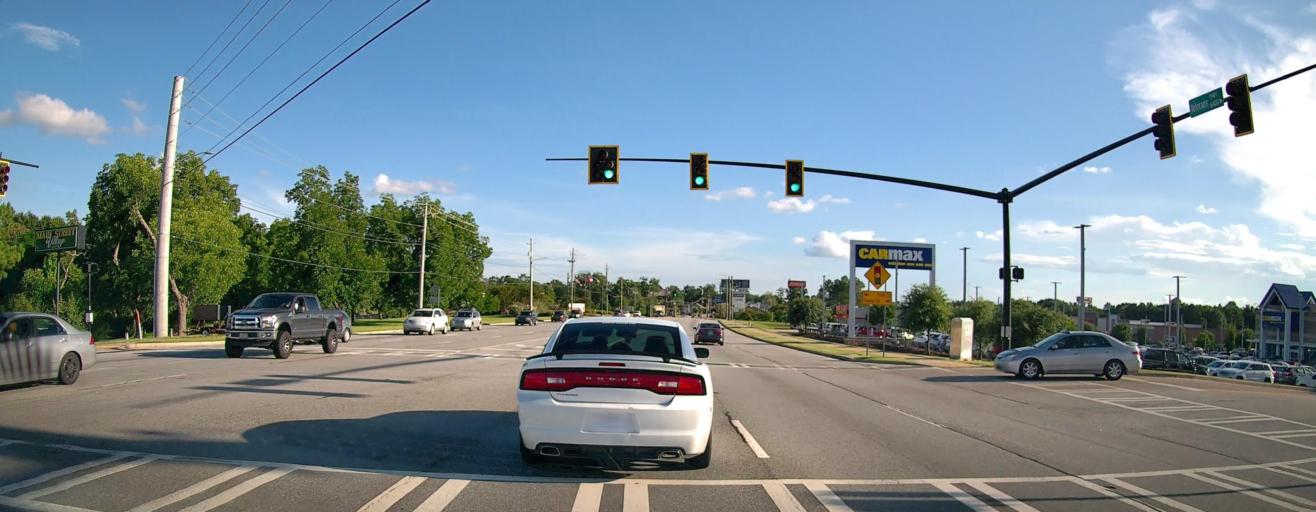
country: US
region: Alabama
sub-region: Russell County
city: Phenix City
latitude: 32.5376
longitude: -84.9547
